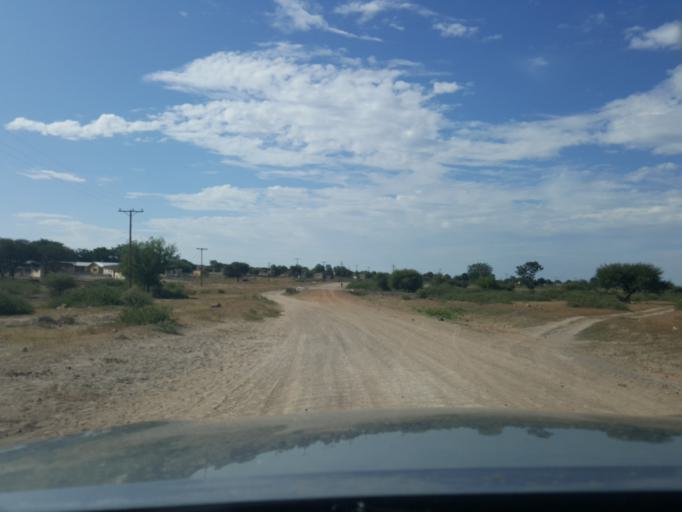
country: BW
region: Kweneng
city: Khudumelapye
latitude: -23.6952
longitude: 24.7173
